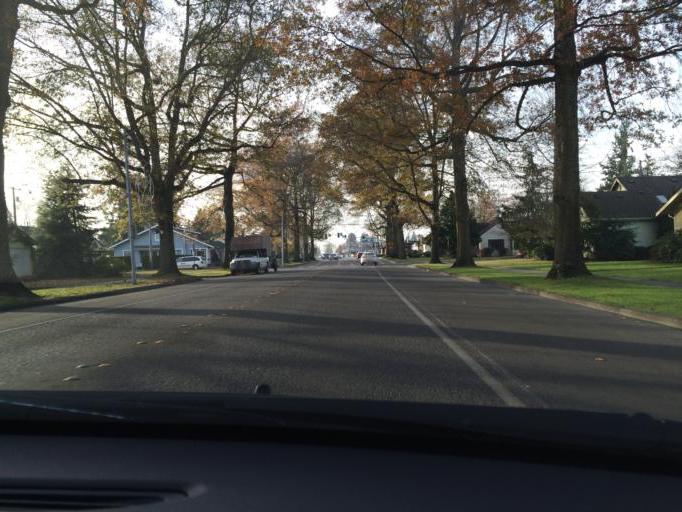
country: US
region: Washington
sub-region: Whatcom County
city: Lynden
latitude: 48.9396
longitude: -122.4667
